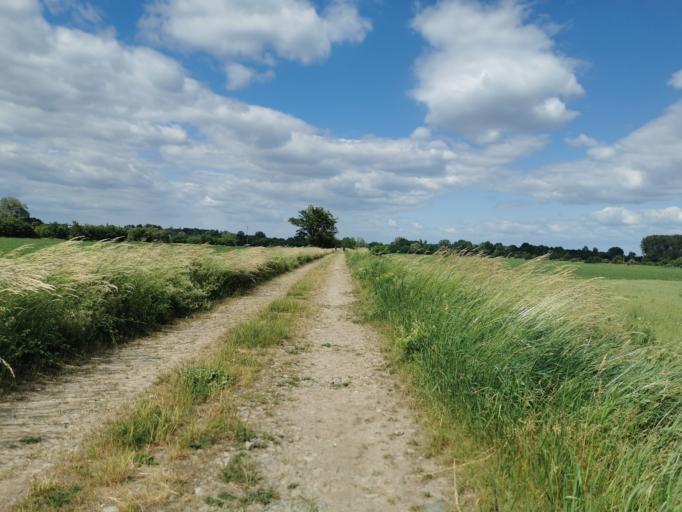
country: CZ
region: South Moravian
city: Rohatec
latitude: 48.8784
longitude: 17.2085
